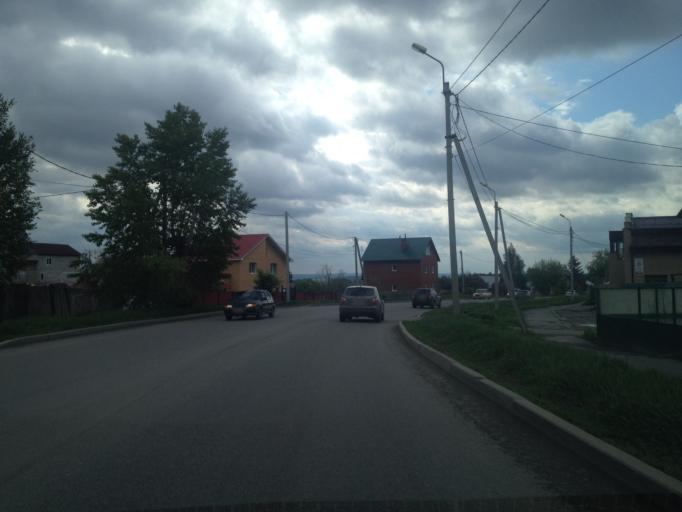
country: RU
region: Sverdlovsk
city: Istok
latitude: 56.7425
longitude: 60.6994
